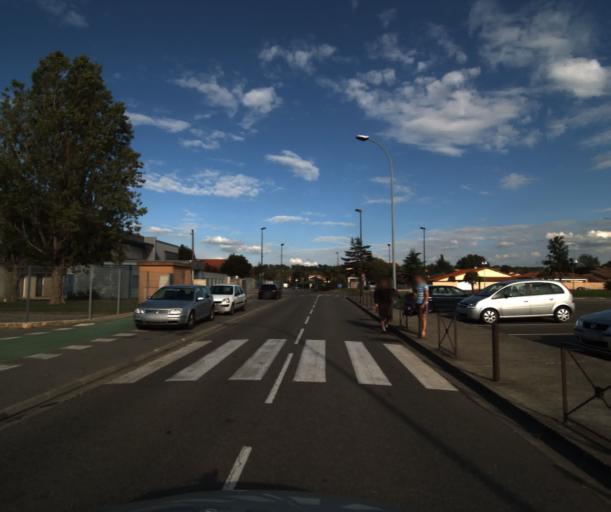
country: FR
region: Midi-Pyrenees
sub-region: Departement de la Haute-Garonne
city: Muret
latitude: 43.4717
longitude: 1.3366
